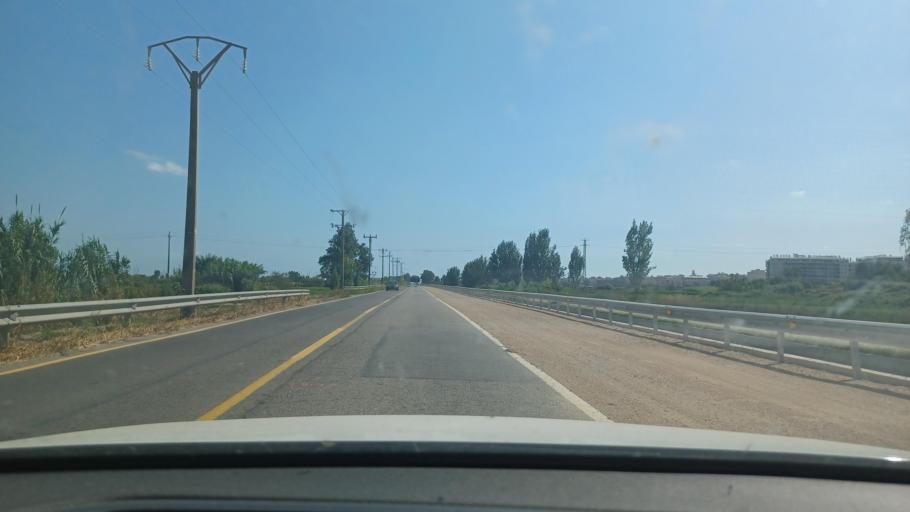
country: ES
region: Catalonia
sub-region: Provincia de Tarragona
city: Sant Carles de la Rapita
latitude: 40.6296
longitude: 0.6008
